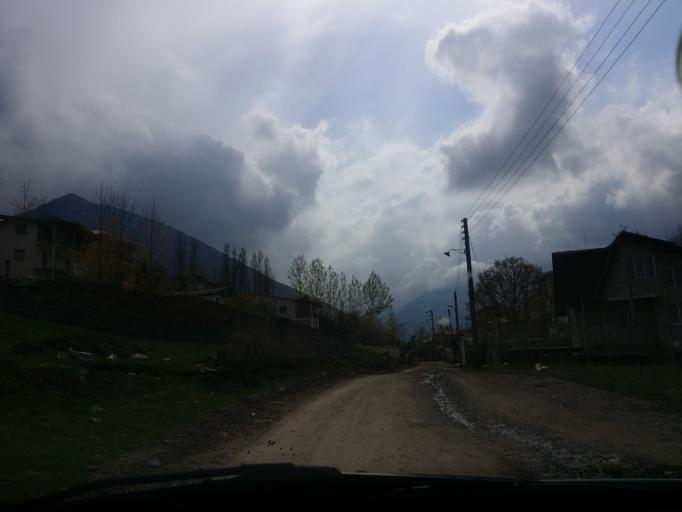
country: IR
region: Mazandaran
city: `Abbasabad
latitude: 36.4870
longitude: 51.1428
